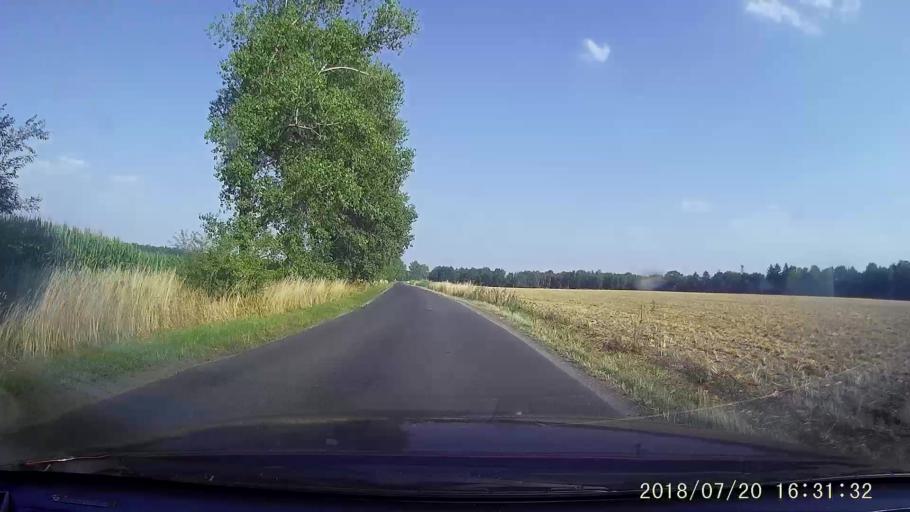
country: PL
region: Lower Silesian Voivodeship
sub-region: Powiat zgorzelecki
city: Sulikow
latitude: 51.0993
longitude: 15.0751
